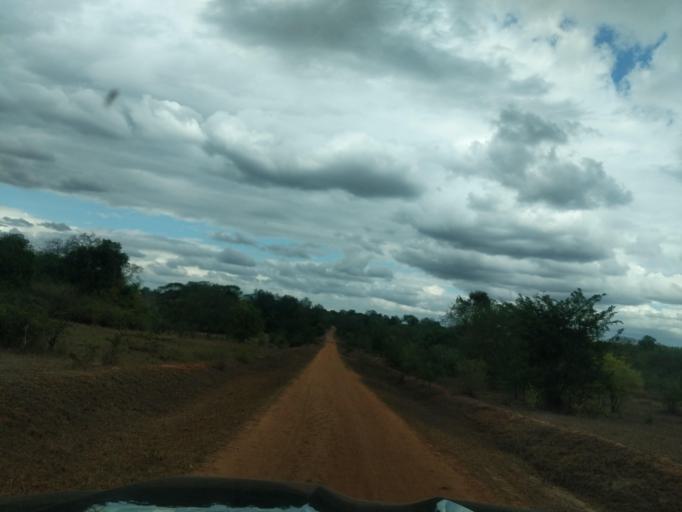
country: TZ
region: Pwani
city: Mvomero
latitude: -5.9357
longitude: 38.4205
